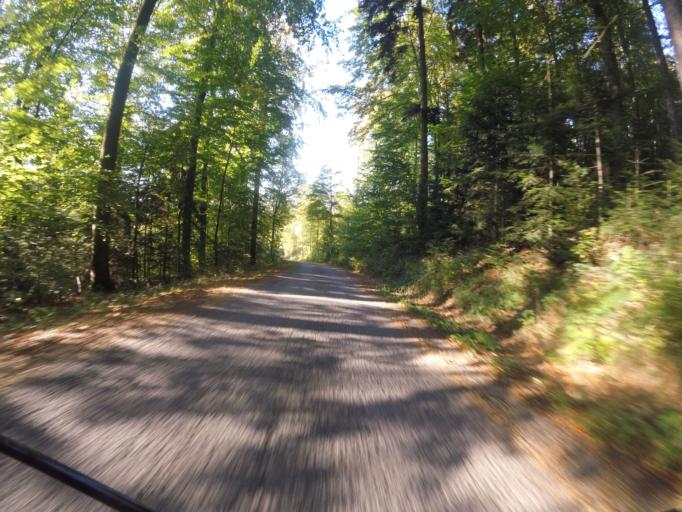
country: DE
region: Baden-Wuerttemberg
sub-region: Regierungsbezirk Stuttgart
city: Spiegelberg
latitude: 49.0075
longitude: 9.4309
